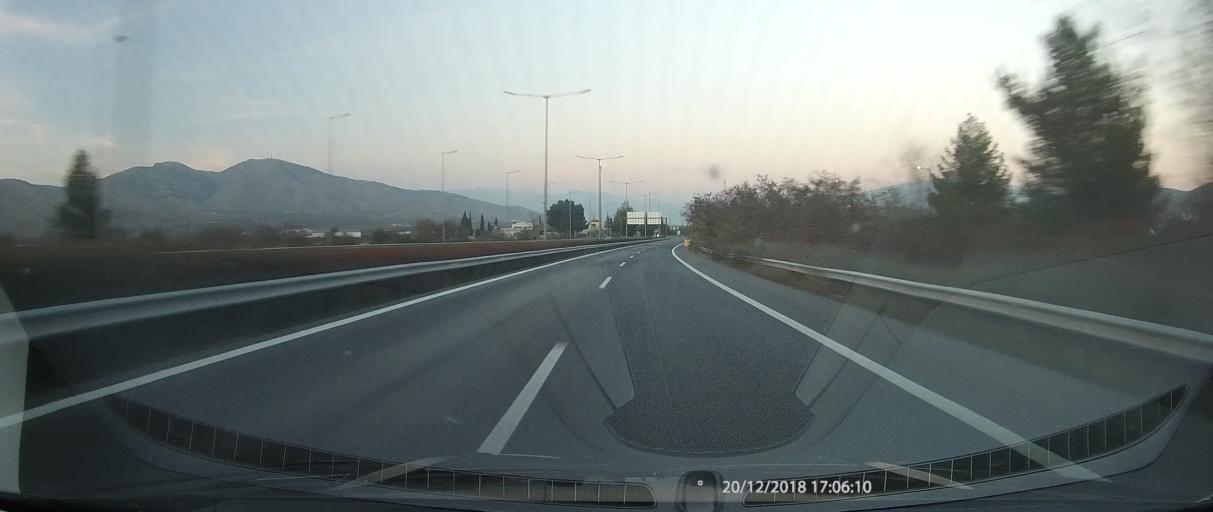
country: GR
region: Thessaly
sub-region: Nomos Larisis
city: Makrychori
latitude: 39.7540
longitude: 22.4755
